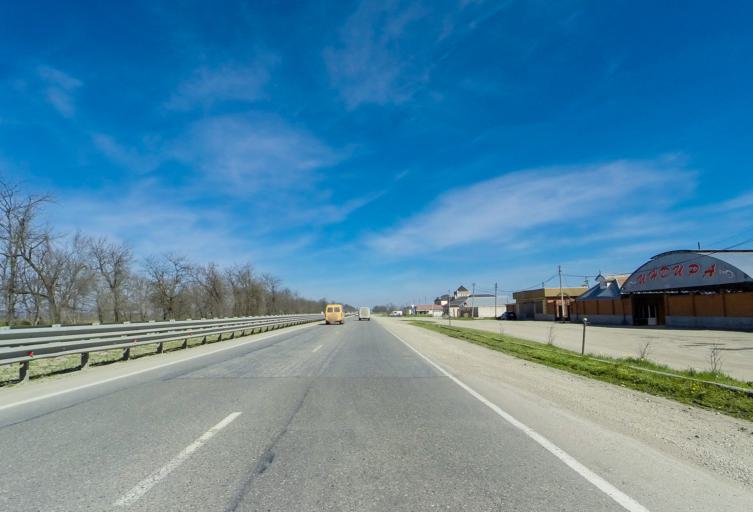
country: RU
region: Kabardino-Balkariya
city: Chegem Vtoroy
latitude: 43.5914
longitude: 43.5763
